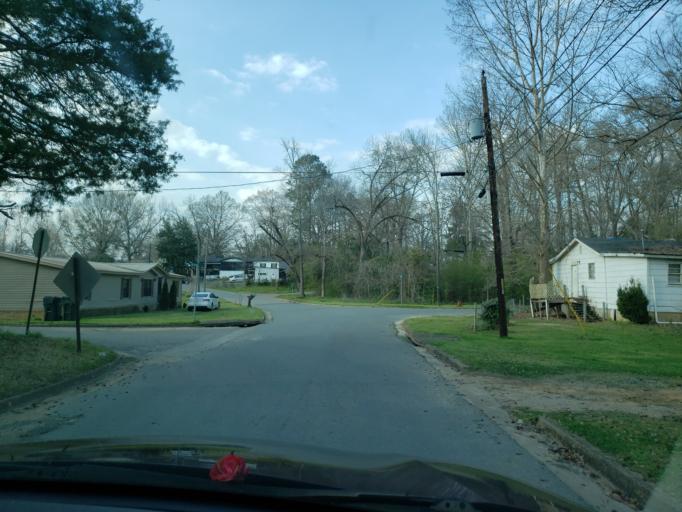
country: US
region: Alabama
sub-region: Hale County
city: Greensboro
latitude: 32.7085
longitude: -87.5991
